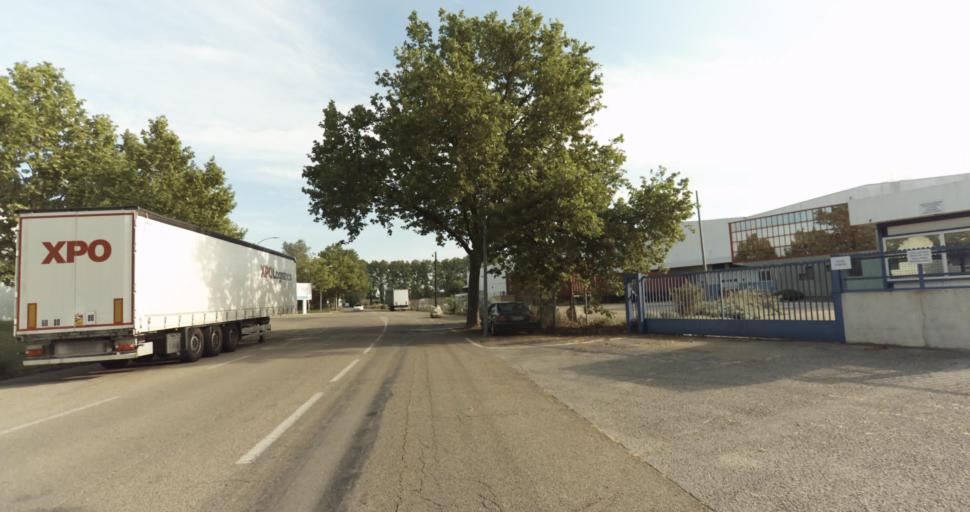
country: FR
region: Languedoc-Roussillon
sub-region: Departement du Gard
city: Rodilhan
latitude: 43.8397
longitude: 4.4168
